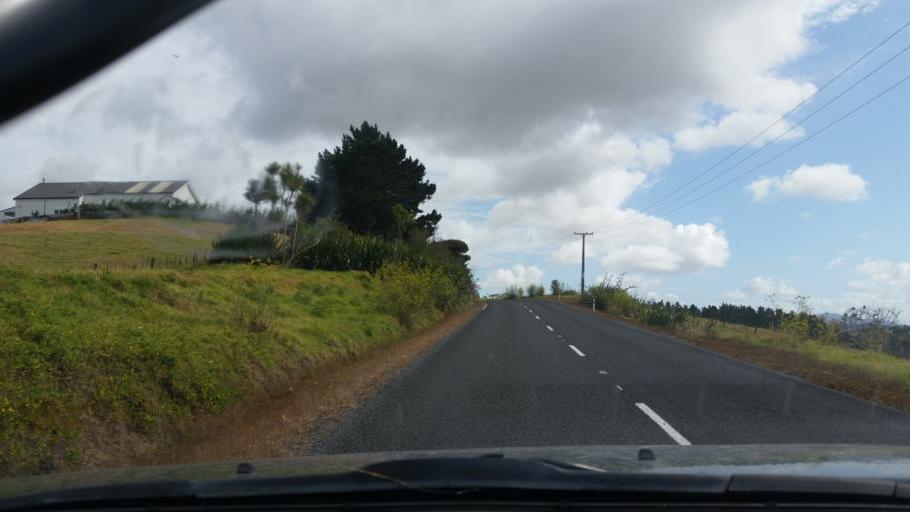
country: NZ
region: Northland
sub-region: Kaipara District
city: Dargaville
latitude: -35.9544
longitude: 173.9223
